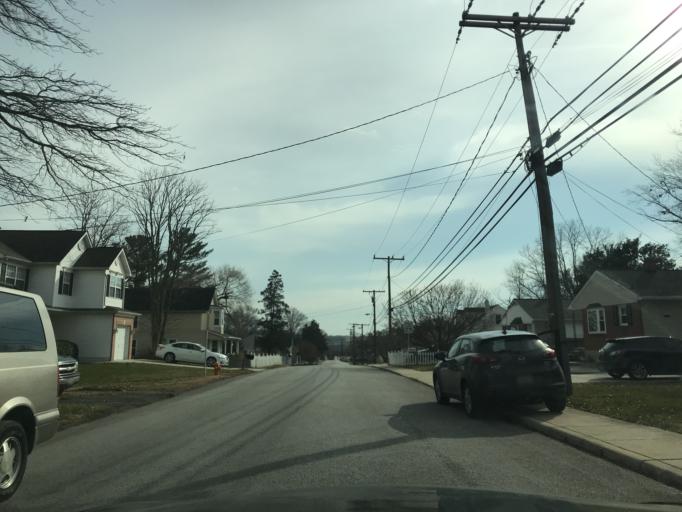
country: US
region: Maryland
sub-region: Howard County
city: Hanover
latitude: 39.1945
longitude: -76.7361
